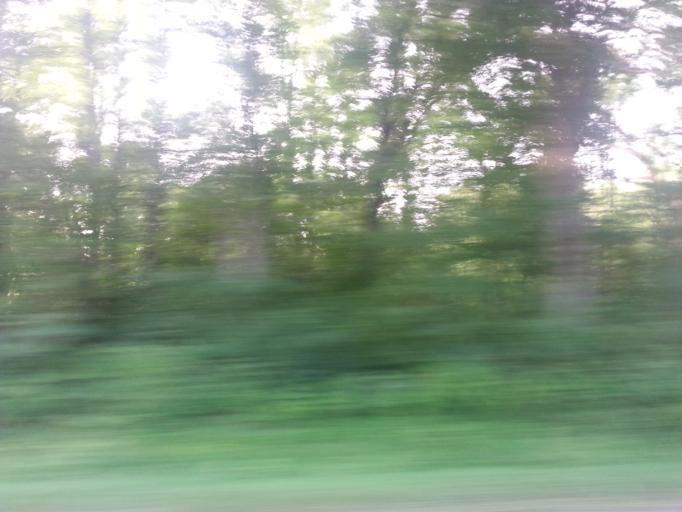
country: US
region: Tennessee
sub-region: Blount County
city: Wildwood
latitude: 35.8417
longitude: -83.8324
